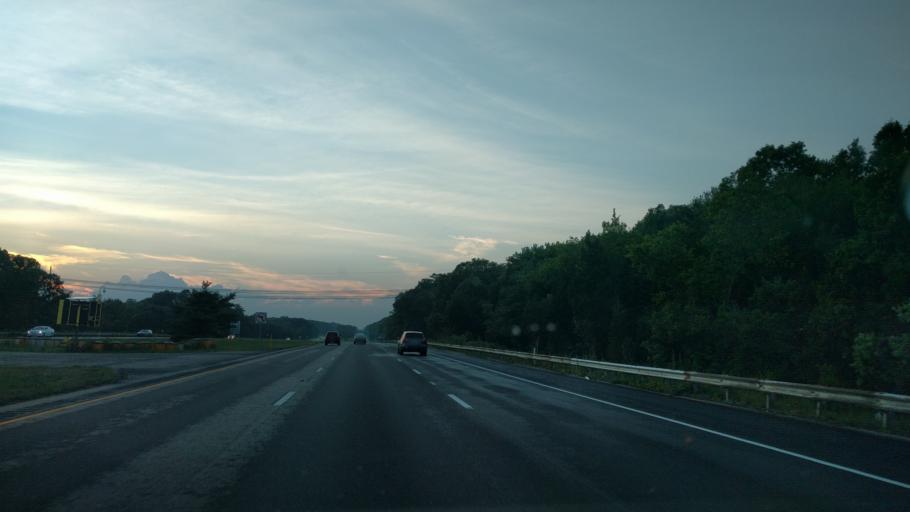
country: US
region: Massachusetts
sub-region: Bristol County
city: Ocean Grove
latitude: 41.7403
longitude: -71.2077
